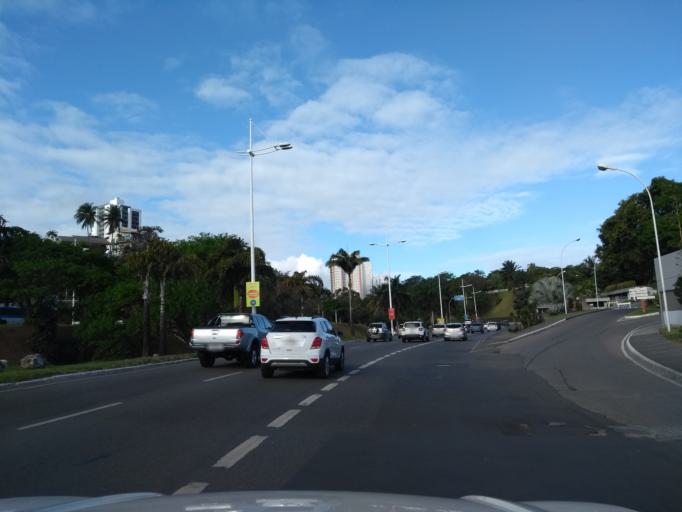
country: BR
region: Bahia
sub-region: Salvador
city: Salvador
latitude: -13.0005
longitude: -38.4820
